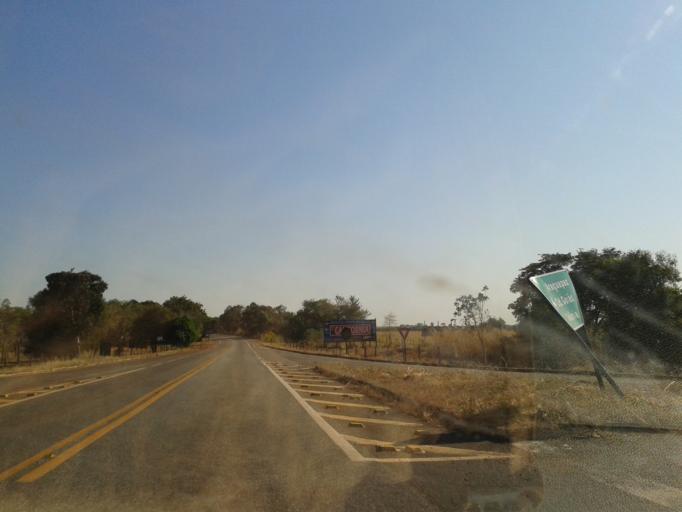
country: BR
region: Goias
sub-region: Mozarlandia
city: Mozarlandia
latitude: -14.8052
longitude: -50.5333
